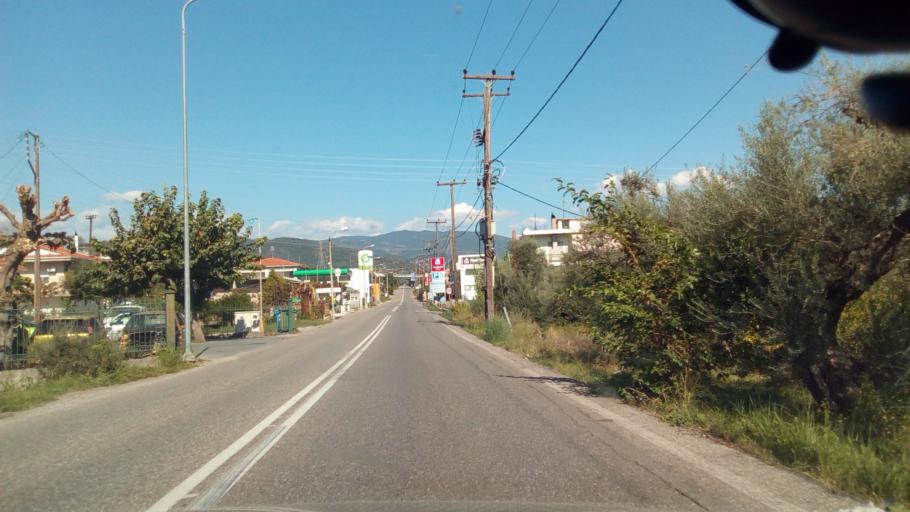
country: GR
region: West Greece
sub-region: Nomos Aitolias kai Akarnanias
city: Nafpaktos
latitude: 38.4041
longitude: 21.8613
